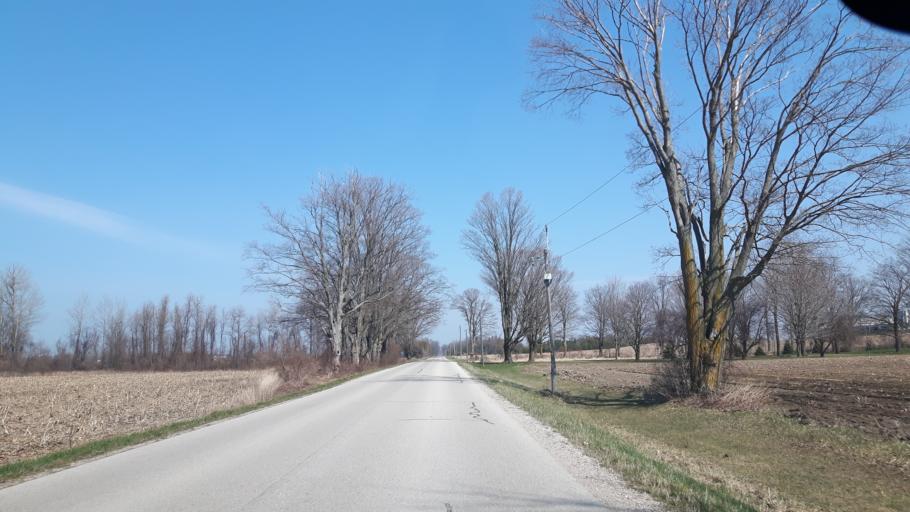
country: CA
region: Ontario
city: Goderich
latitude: 43.6779
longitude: -81.6847
